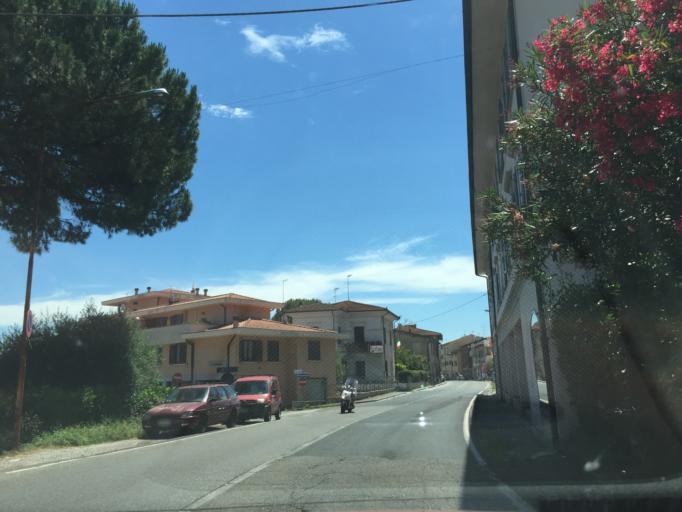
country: IT
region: Tuscany
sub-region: Province of Pisa
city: San Miniato
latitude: 43.6879
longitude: 10.7898
